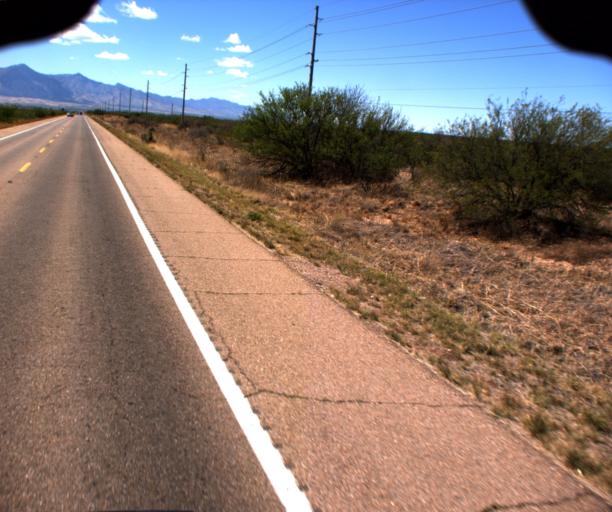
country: US
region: Arizona
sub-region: Cochise County
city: Naco
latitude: 31.3772
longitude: -110.0170
